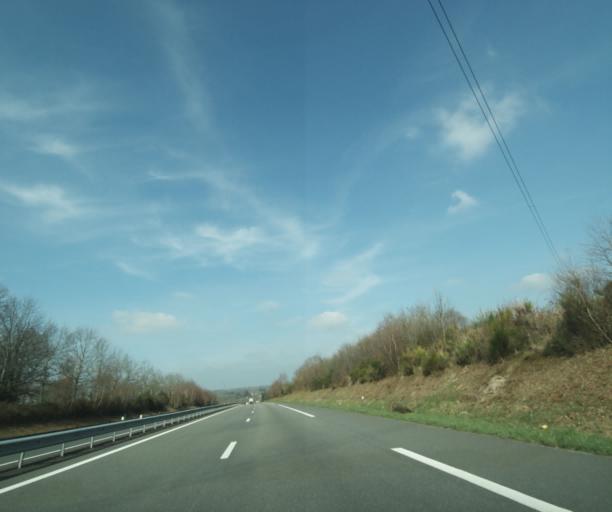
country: FR
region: Limousin
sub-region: Departement de la Haute-Vienne
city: Saint-Sulpice-les-Feuilles
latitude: 46.3293
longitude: 1.4186
